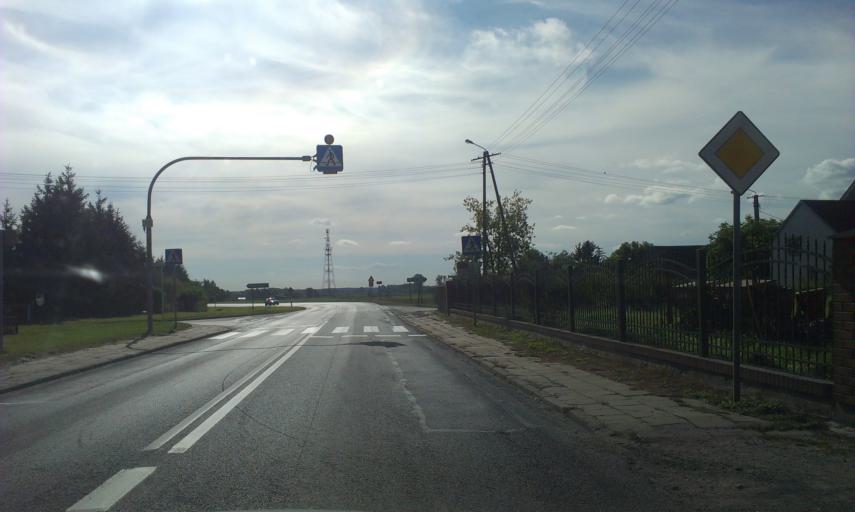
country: PL
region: Greater Poland Voivodeship
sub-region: Powiat zlotowski
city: Okonek
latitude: 53.6063
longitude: 16.7978
